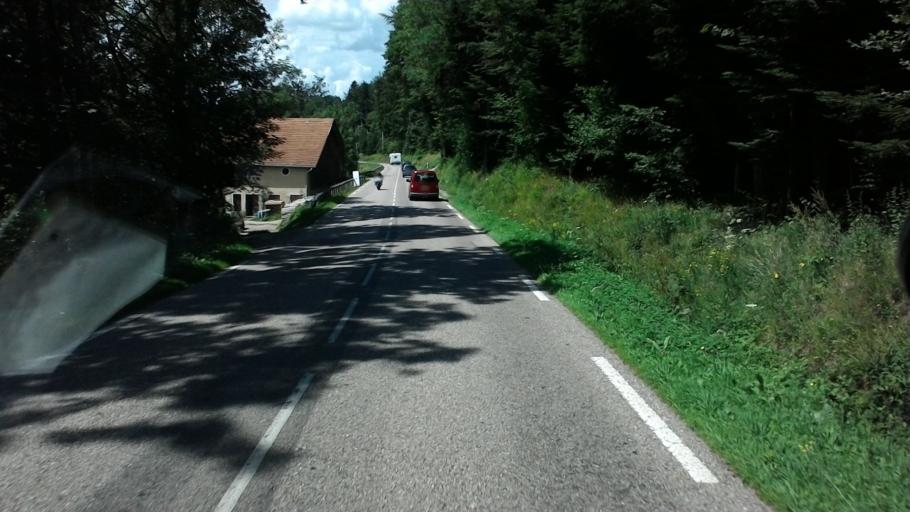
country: FR
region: Lorraine
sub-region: Departement des Vosges
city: Le Tholy
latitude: 48.0976
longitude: 6.7148
